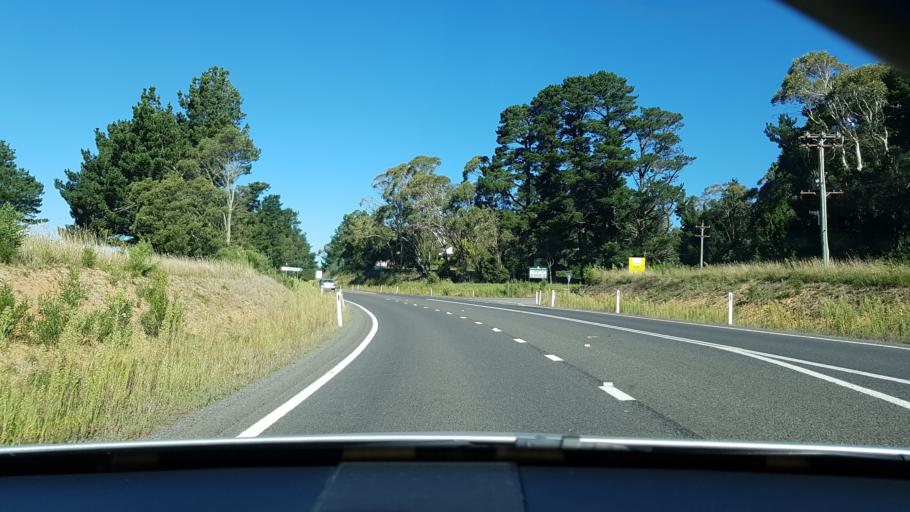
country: AU
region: New South Wales
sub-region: Lithgow
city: Bowenfels
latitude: -33.6469
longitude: 150.0481
